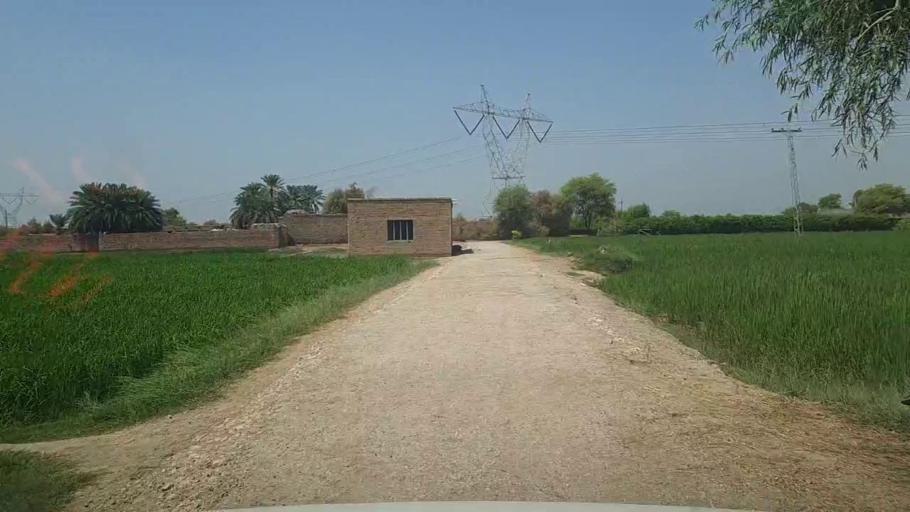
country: PK
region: Sindh
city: Kandhkot
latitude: 28.3194
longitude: 69.3761
